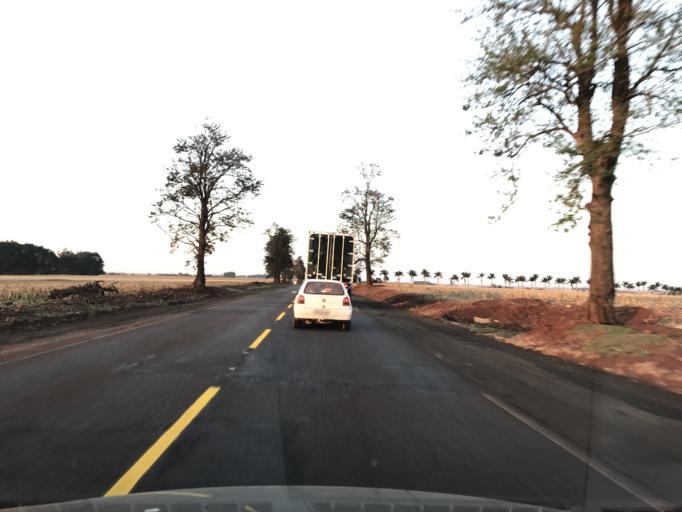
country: BR
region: Parana
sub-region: Palotina
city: Palotina
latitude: -24.4026
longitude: -53.8577
